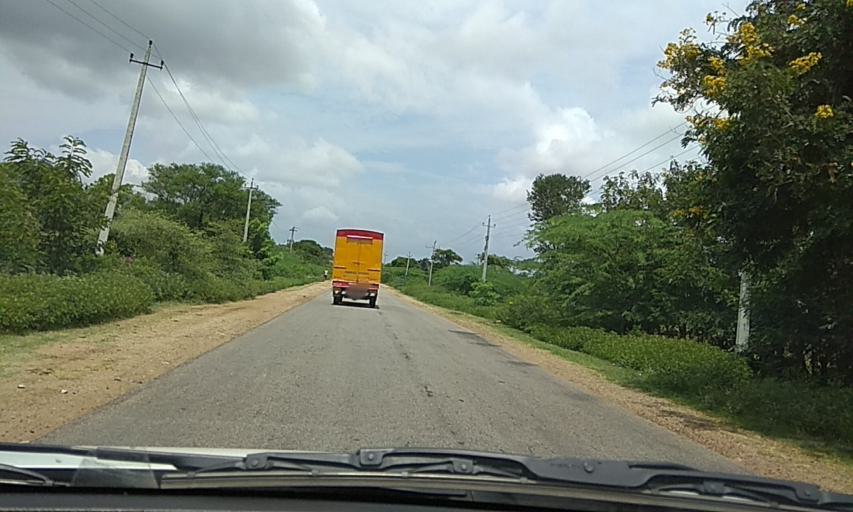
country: IN
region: Karnataka
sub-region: Chamrajnagar
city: Gundlupet
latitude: 11.8138
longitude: 76.7648
